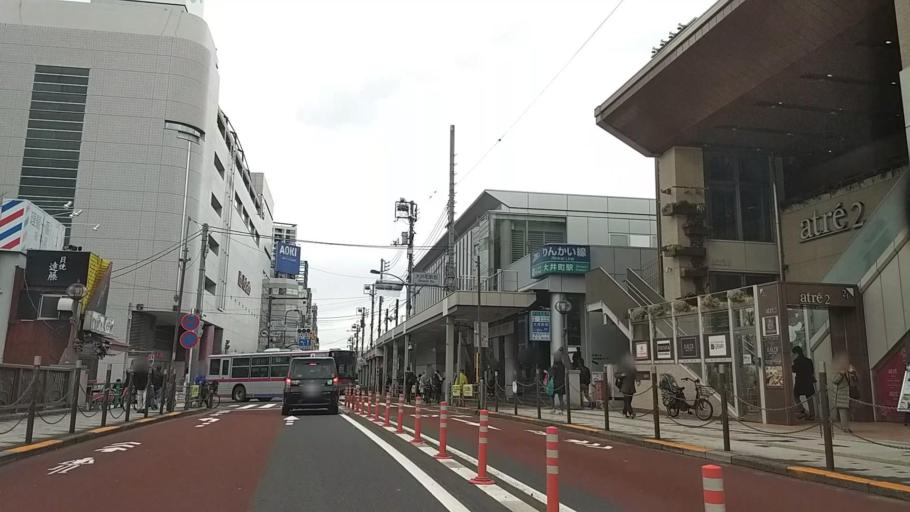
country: JP
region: Kanagawa
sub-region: Kawasaki-shi
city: Kawasaki
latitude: 35.6074
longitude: 139.7351
